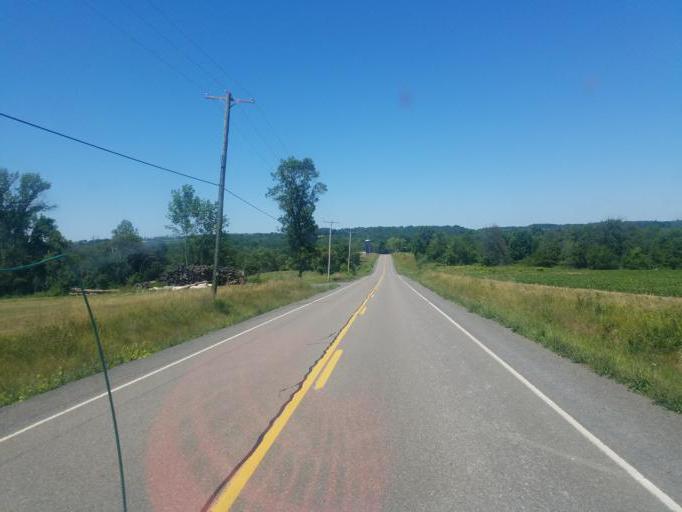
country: US
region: New York
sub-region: Yates County
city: Penn Yan
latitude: 42.6551
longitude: -77.0008
